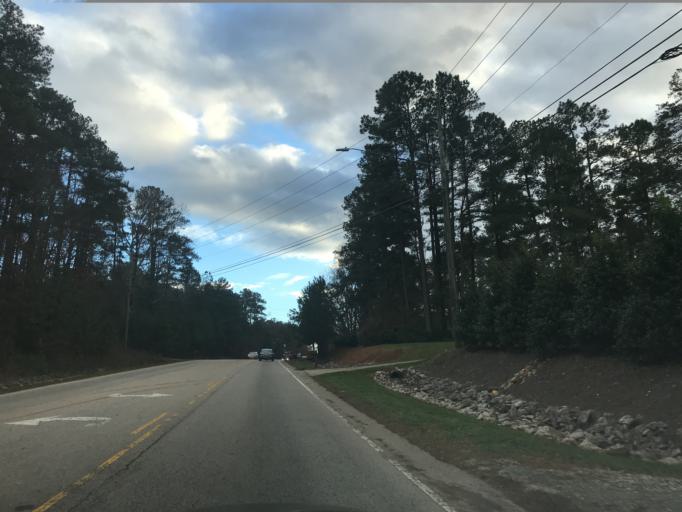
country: US
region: North Carolina
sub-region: Wake County
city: West Raleigh
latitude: 35.8517
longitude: -78.6728
